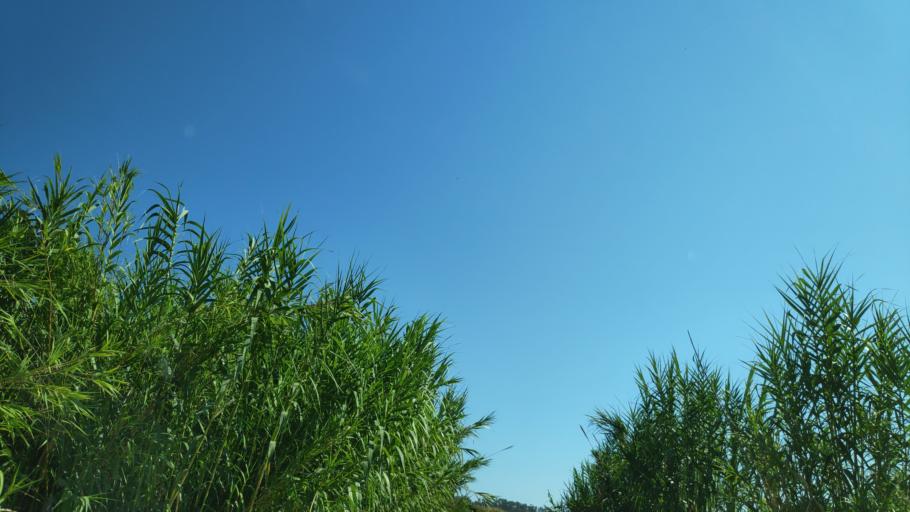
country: IT
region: Calabria
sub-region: Provincia di Reggio Calabria
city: Monasterace
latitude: 38.4341
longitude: 16.5252
